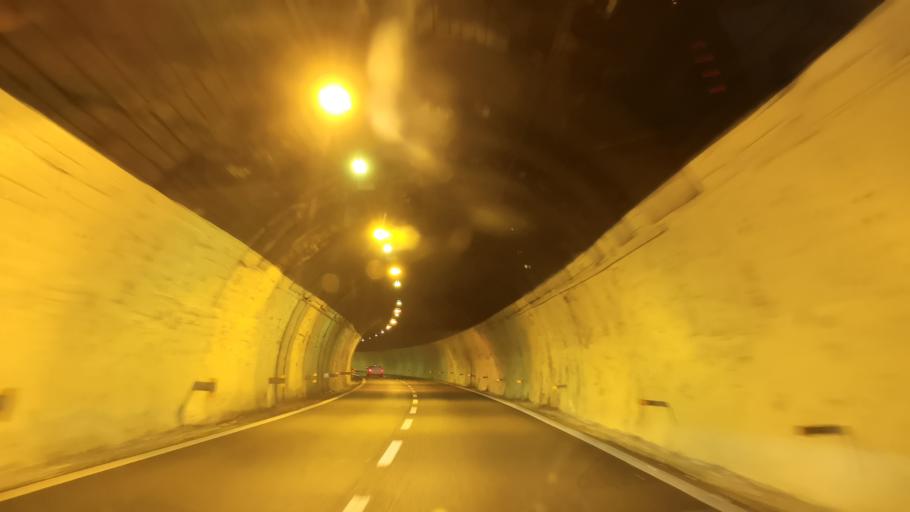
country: IT
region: Lombardy
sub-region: Provincia di Como
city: San Fermo della Battaglia
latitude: 45.8243
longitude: 9.0463
